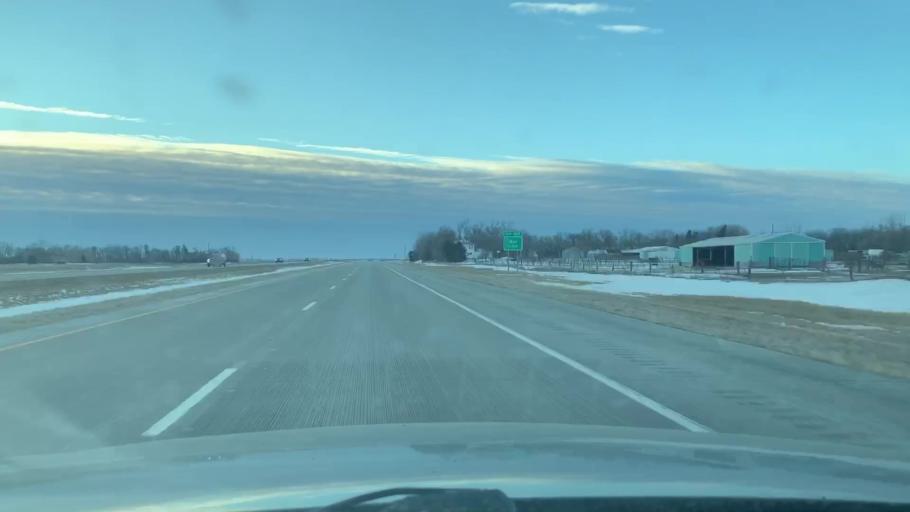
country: US
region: North Dakota
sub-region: Cass County
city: Casselton
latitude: 46.8758
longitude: -97.4655
